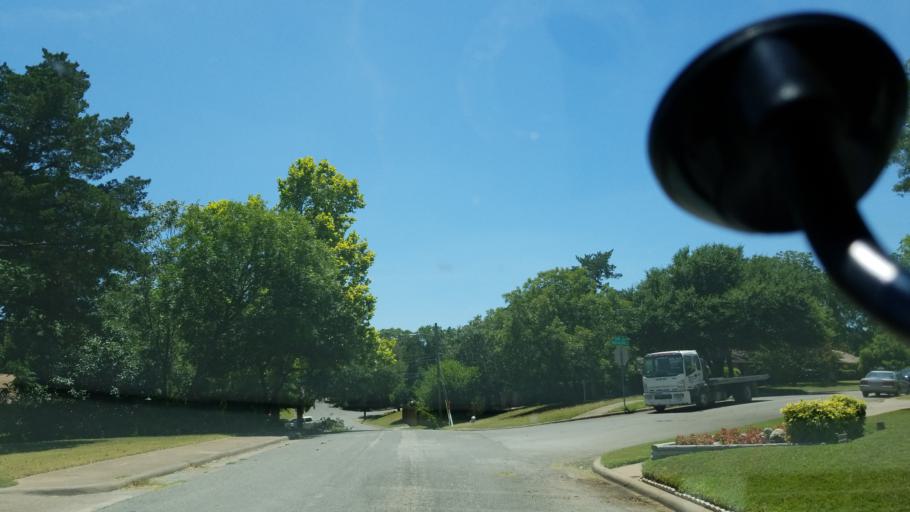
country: US
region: Texas
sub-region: Dallas County
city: Cockrell Hill
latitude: 32.6900
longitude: -96.8351
